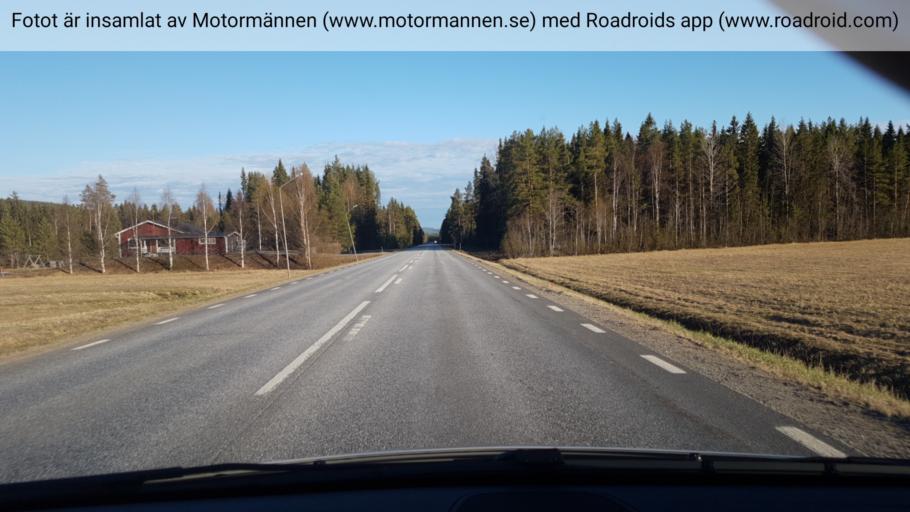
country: SE
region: Vaesterbotten
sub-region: Vannas Kommun
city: Vaennaes
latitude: 63.9616
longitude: 19.7522
